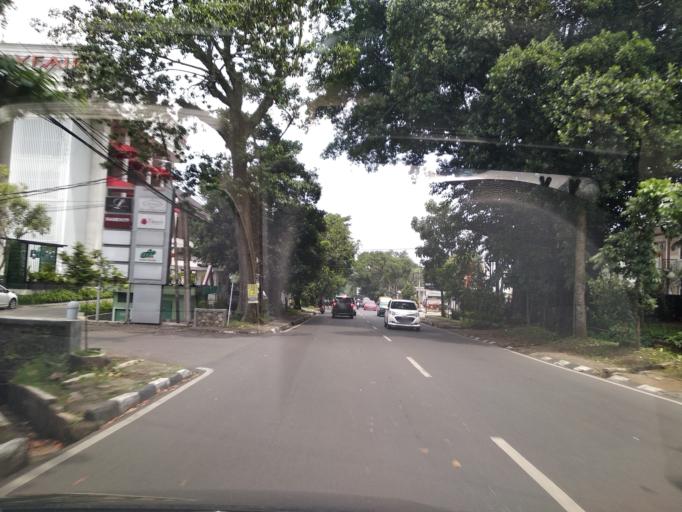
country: ID
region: West Java
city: Bandung
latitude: -6.8791
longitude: 107.5963
